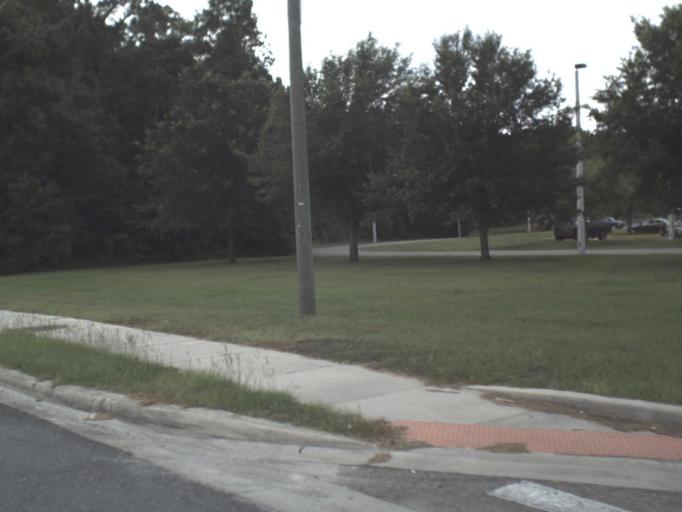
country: US
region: Florida
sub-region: Taylor County
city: Perry
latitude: 30.1210
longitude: -83.5919
